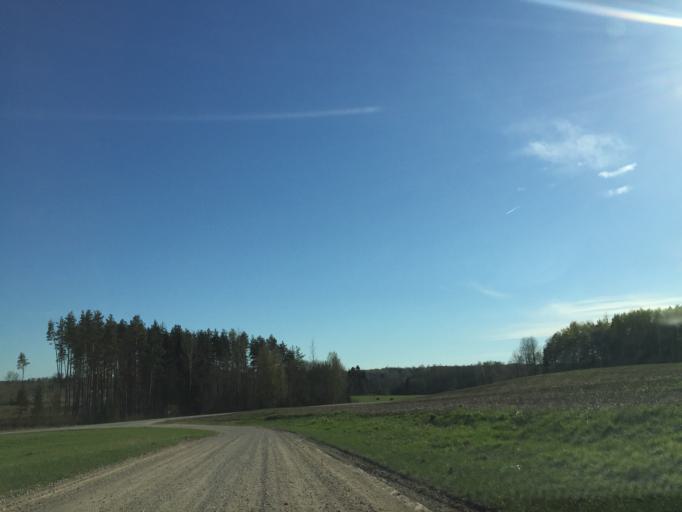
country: EE
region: Valgamaa
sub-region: Valga linn
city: Valga
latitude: 57.7585
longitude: 26.2009
